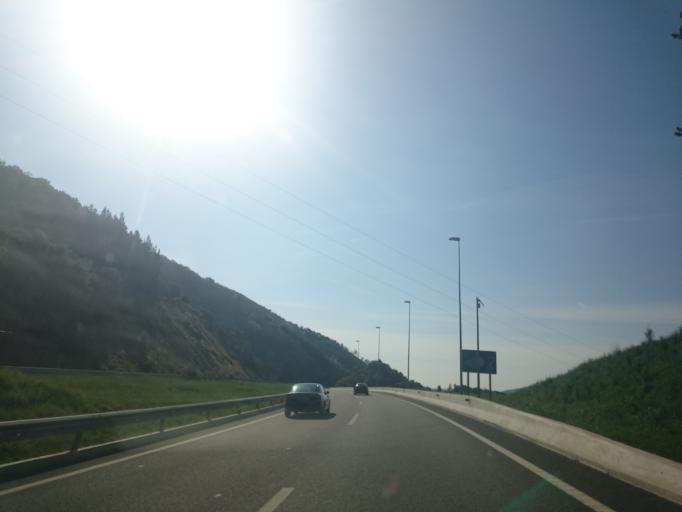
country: ES
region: Catalonia
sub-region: Provincia de Girona
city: Viladrau
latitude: 41.8508
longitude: 2.4545
